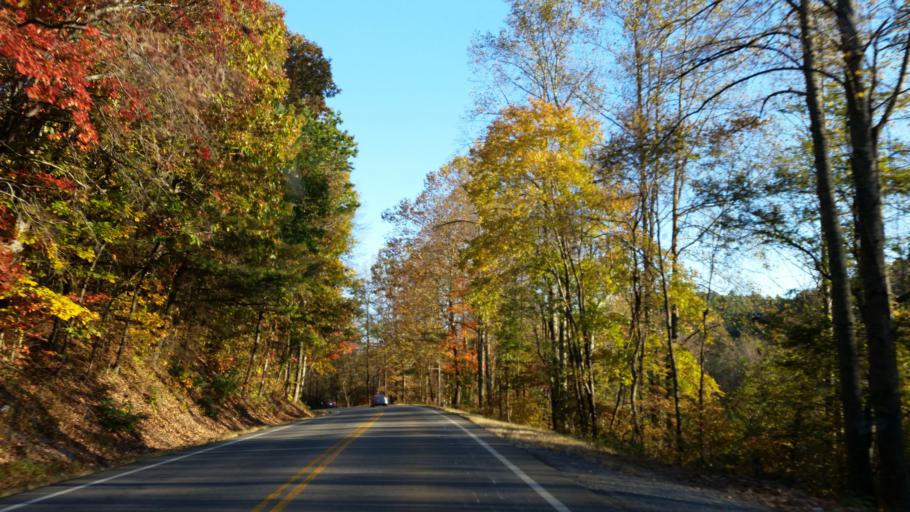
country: US
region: Georgia
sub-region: Pickens County
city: Jasper
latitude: 34.5647
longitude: -84.3068
